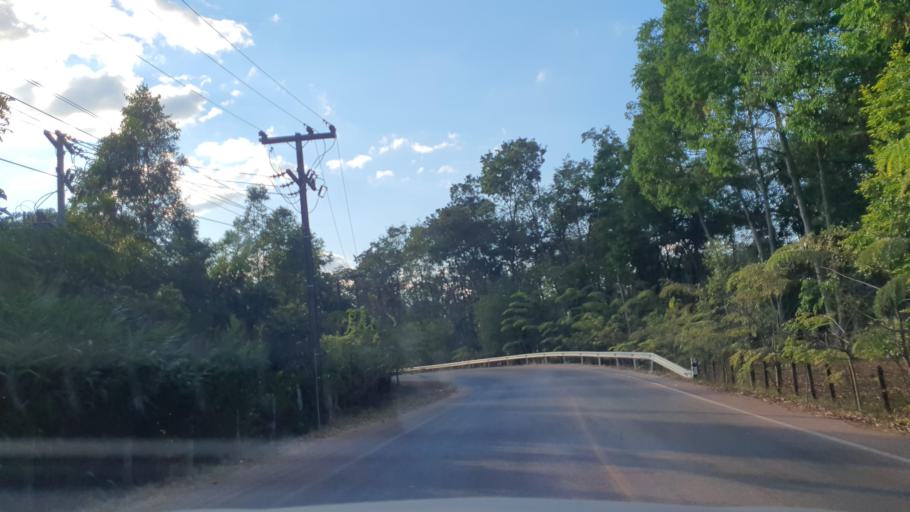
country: TH
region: Changwat Bueng Kan
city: Si Wilai
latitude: 18.1287
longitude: 103.8815
